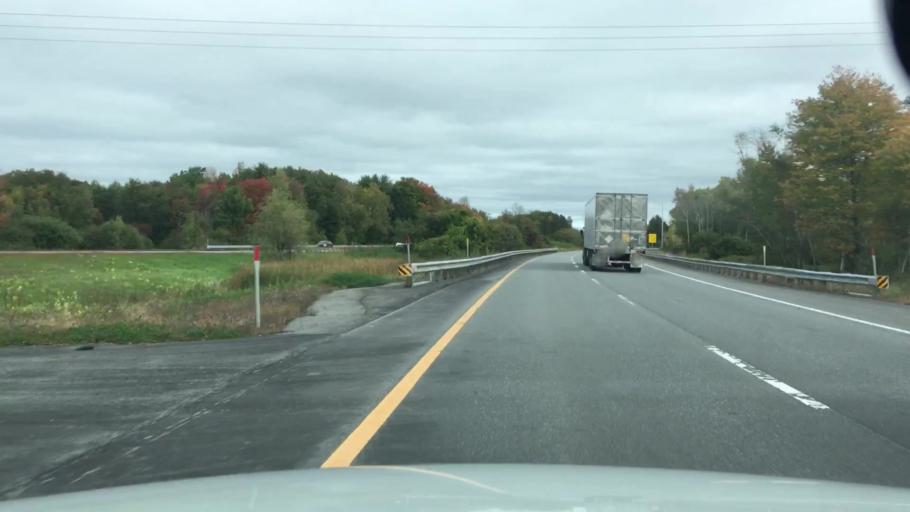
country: US
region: Maine
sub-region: Penobscot County
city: Newport
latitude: 44.8359
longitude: -69.2997
